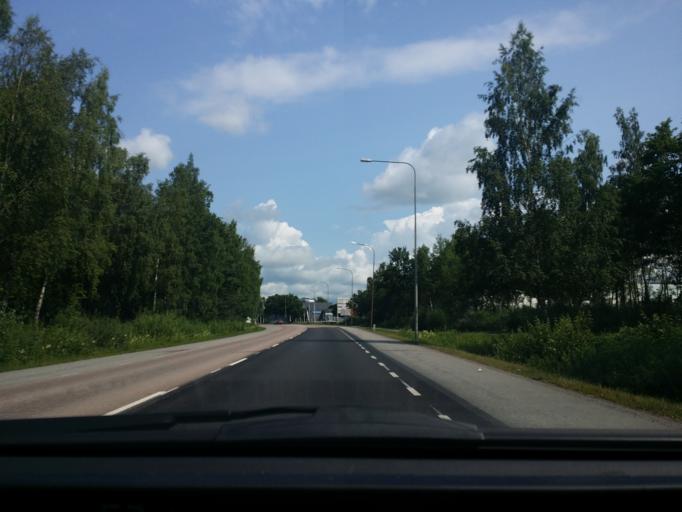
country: SE
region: Vaestmanland
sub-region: Vasteras
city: Vasteras
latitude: 59.6111
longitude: 16.6011
